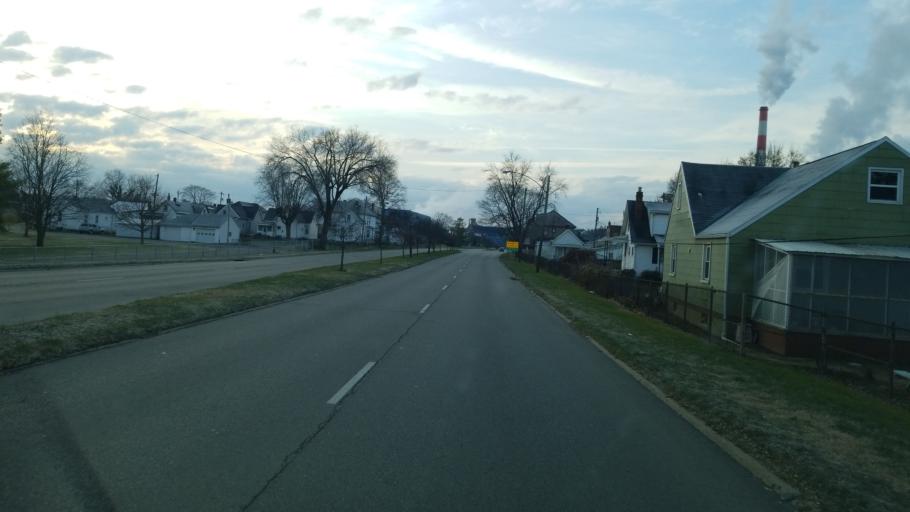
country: US
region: Ohio
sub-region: Ross County
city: Chillicothe
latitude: 39.3319
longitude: -82.9737
